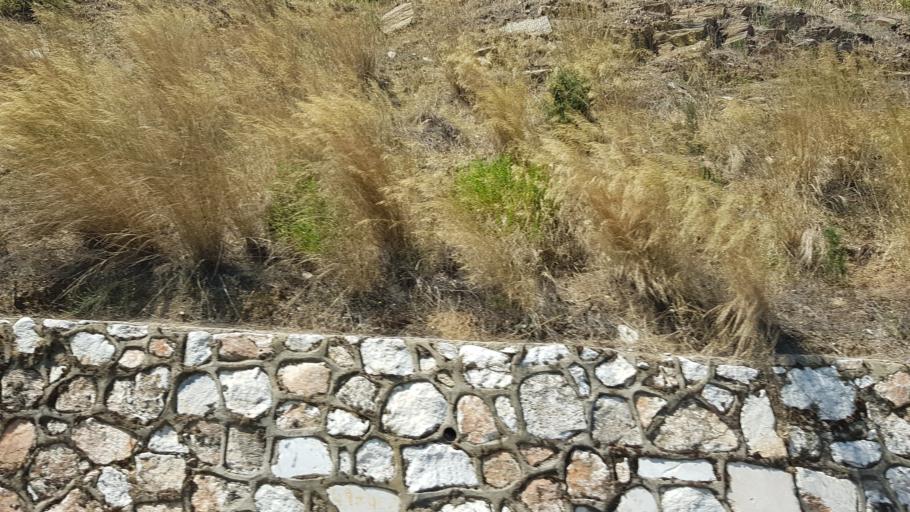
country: TR
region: Aydin
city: Akcaova
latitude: 37.5087
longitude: 28.1016
